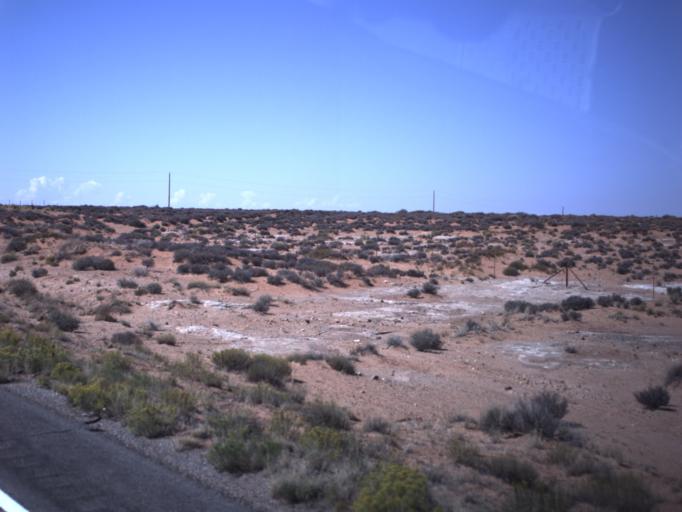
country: US
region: Utah
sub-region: San Juan County
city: Blanding
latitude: 37.0415
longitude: -109.5811
